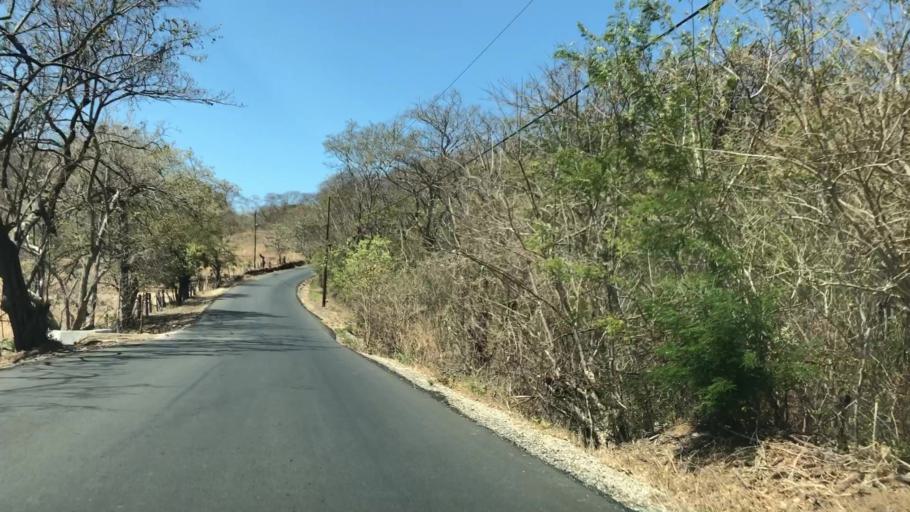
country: CR
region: Guanacaste
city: Belen
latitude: 10.3503
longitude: -85.8195
